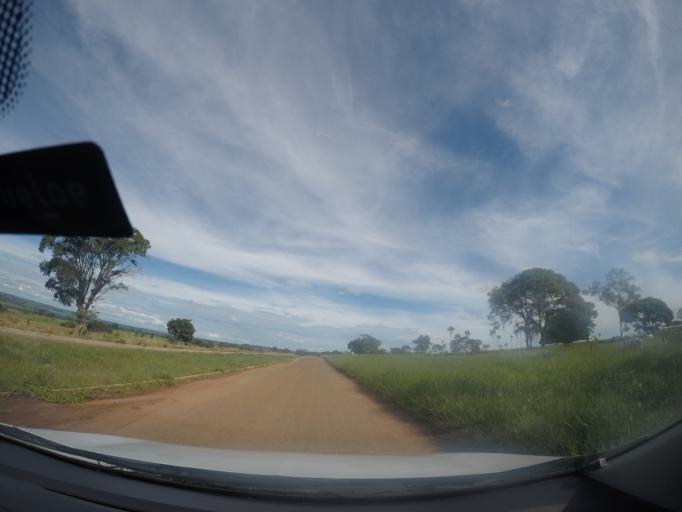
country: BR
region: Goias
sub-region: Inhumas
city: Inhumas
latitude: -16.4001
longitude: -49.4718
